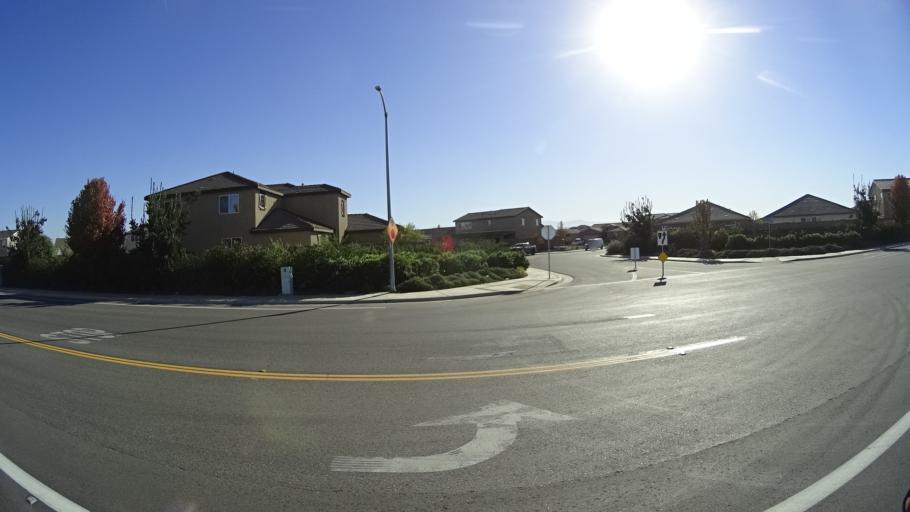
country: US
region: California
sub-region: Kern County
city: Greenfield
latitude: 35.2815
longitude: -119.0677
